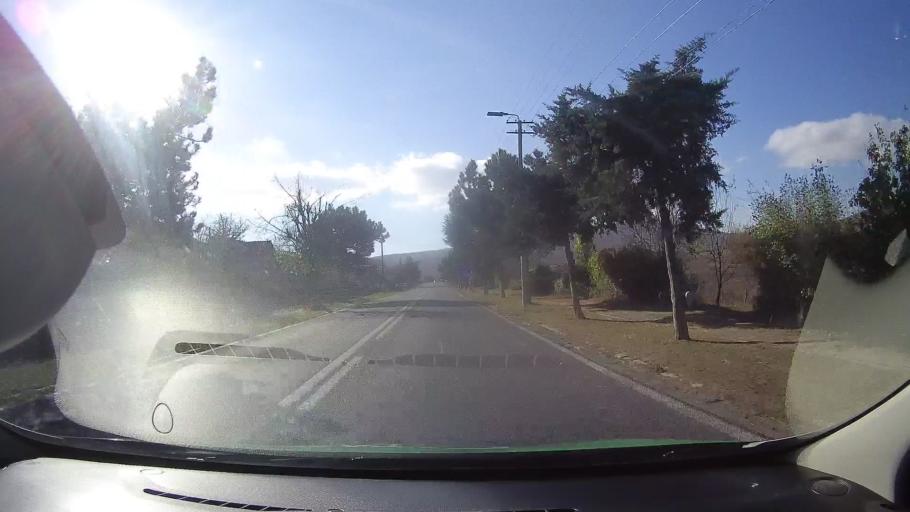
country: RO
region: Tulcea
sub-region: Oras Babadag
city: Babadag
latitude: 44.8809
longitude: 28.6936
